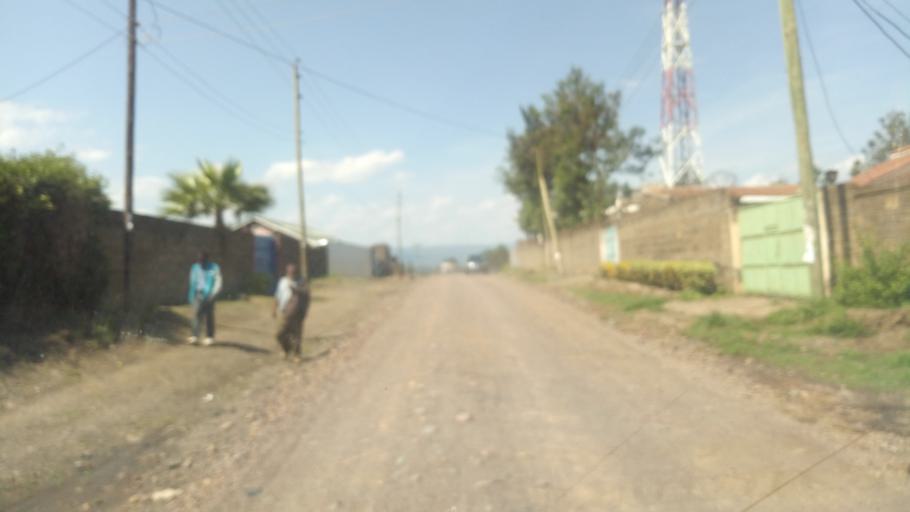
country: KE
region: Nakuru
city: Nakuru
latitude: -0.2767
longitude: 36.1085
